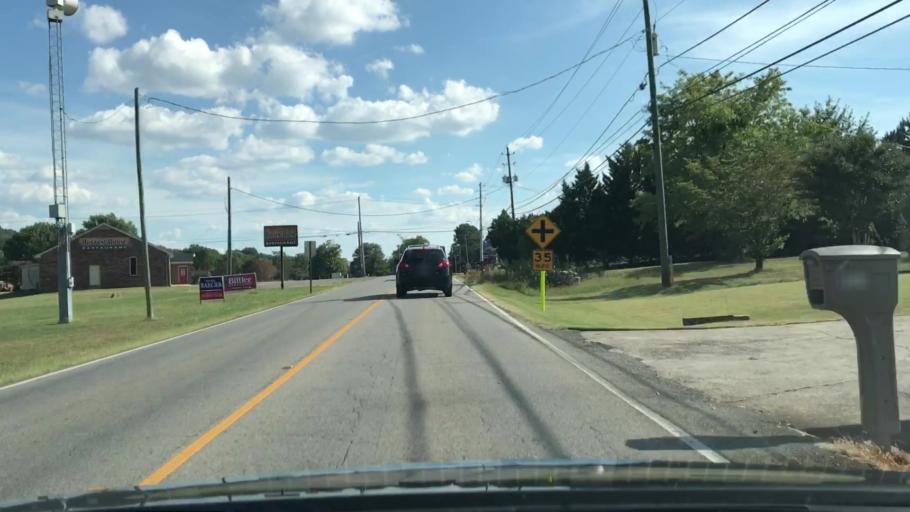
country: US
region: Alabama
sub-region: Madison County
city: Harvest
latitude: 34.8318
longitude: -86.7492
